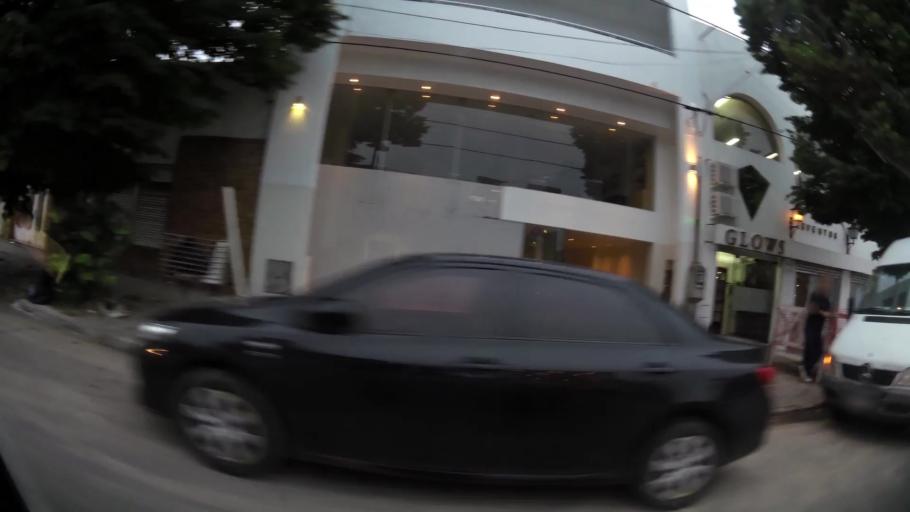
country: AR
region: Buenos Aires
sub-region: Partido de La Plata
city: La Plata
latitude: -34.8995
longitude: -57.9705
